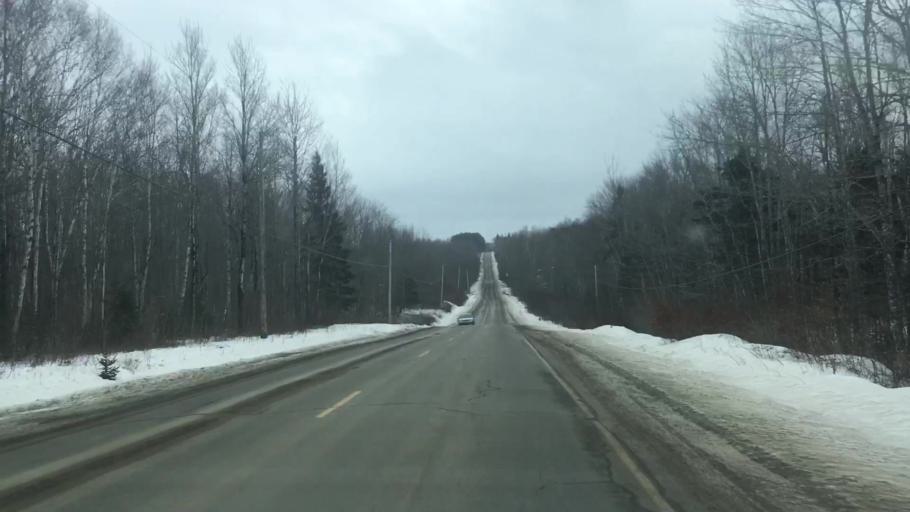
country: US
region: Maine
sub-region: Washington County
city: East Machias
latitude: 44.9697
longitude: -67.4471
